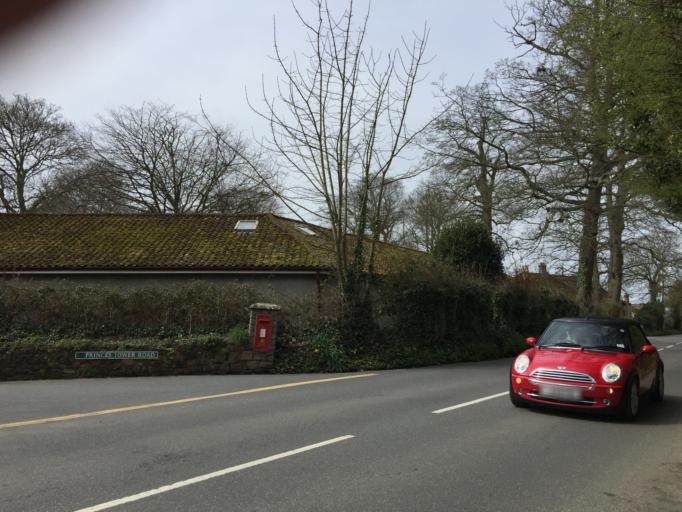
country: JE
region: St Helier
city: Saint Helier
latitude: 49.2008
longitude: -2.0632
